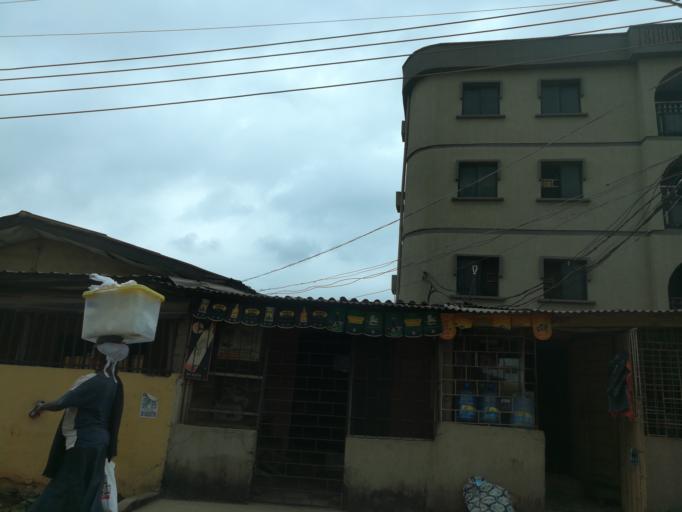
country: NG
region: Lagos
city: Oshodi
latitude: 6.5562
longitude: 3.3348
